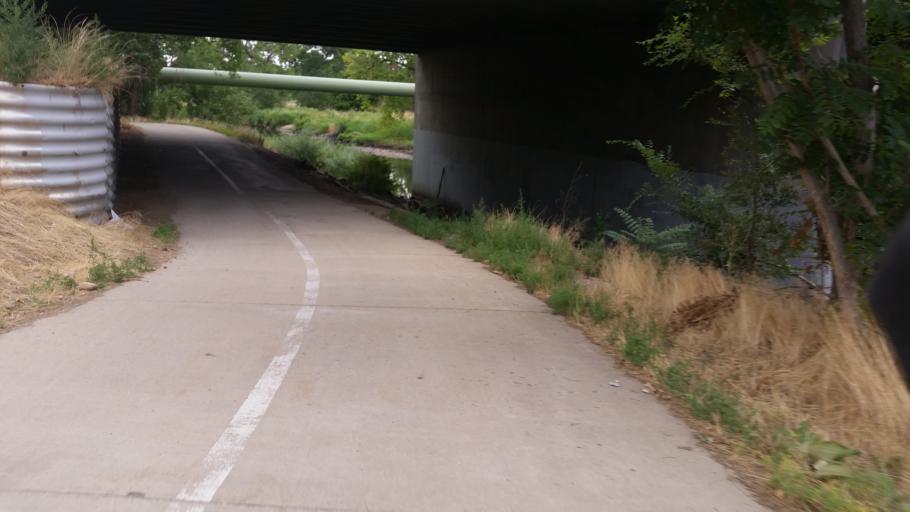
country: US
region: Colorado
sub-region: Adams County
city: Welby
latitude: 39.8229
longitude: -104.9783
